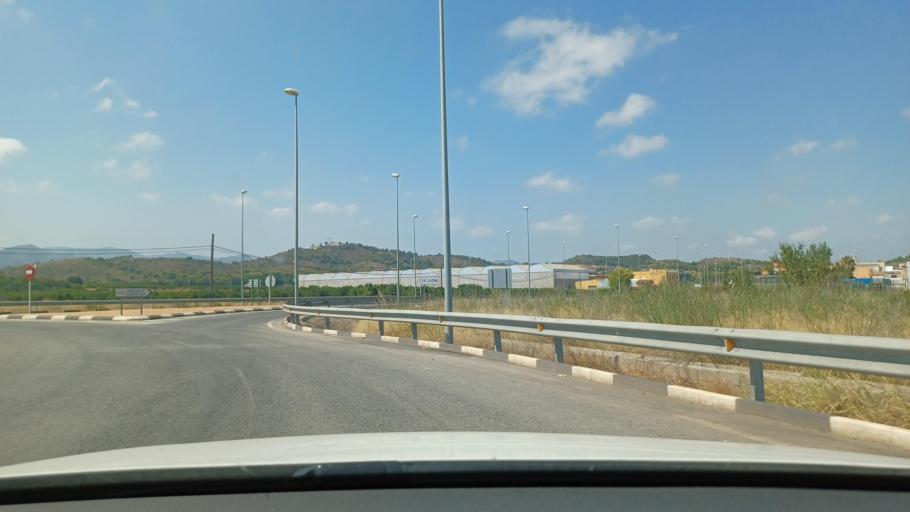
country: ES
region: Valencia
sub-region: Provincia de Castello
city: Almenara
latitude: 39.7665
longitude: -0.2091
